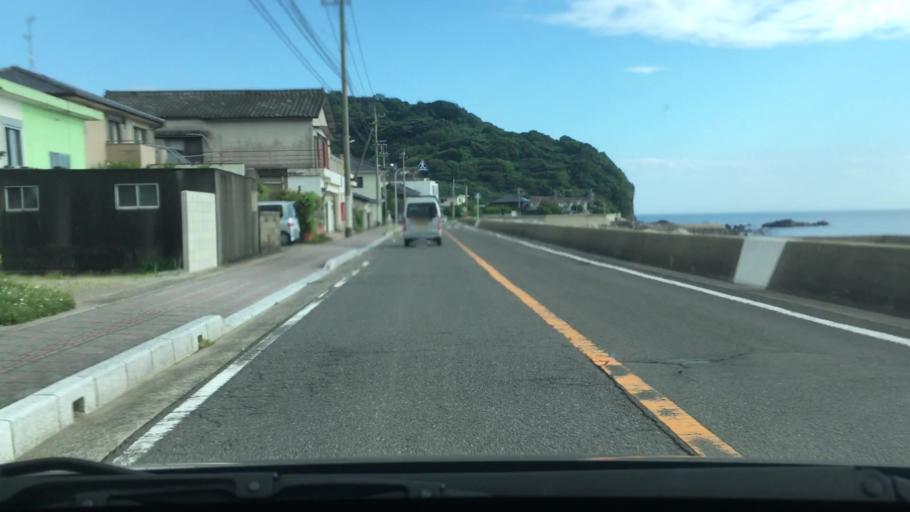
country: JP
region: Nagasaki
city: Togitsu
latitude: 32.8321
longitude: 129.7189
